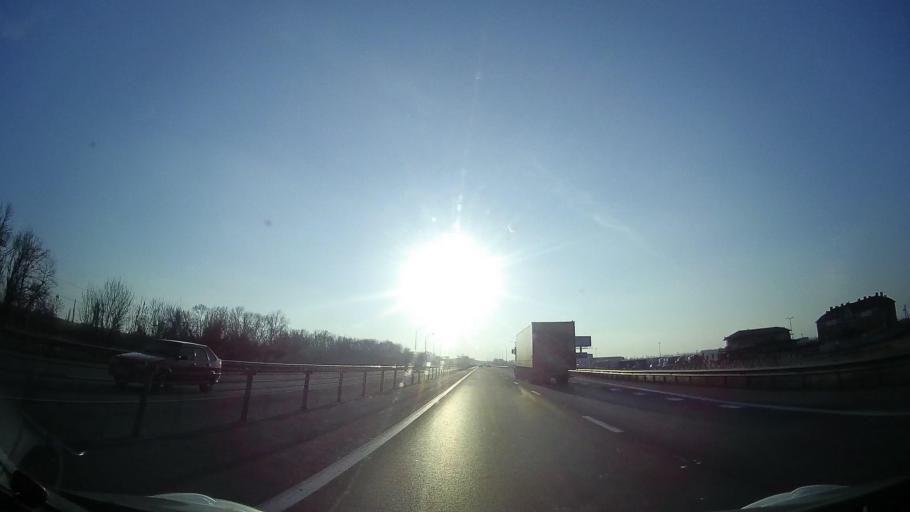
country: RU
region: Rostov
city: Ol'ginskaya
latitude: 47.1231
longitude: 39.8679
